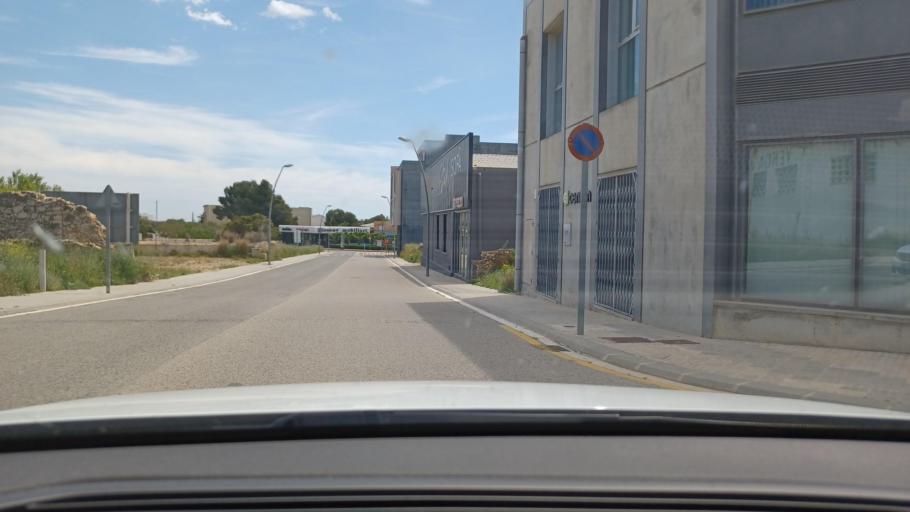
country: ES
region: Valencia
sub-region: Provincia de Castello
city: Rosell
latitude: 40.6333
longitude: 0.2893
